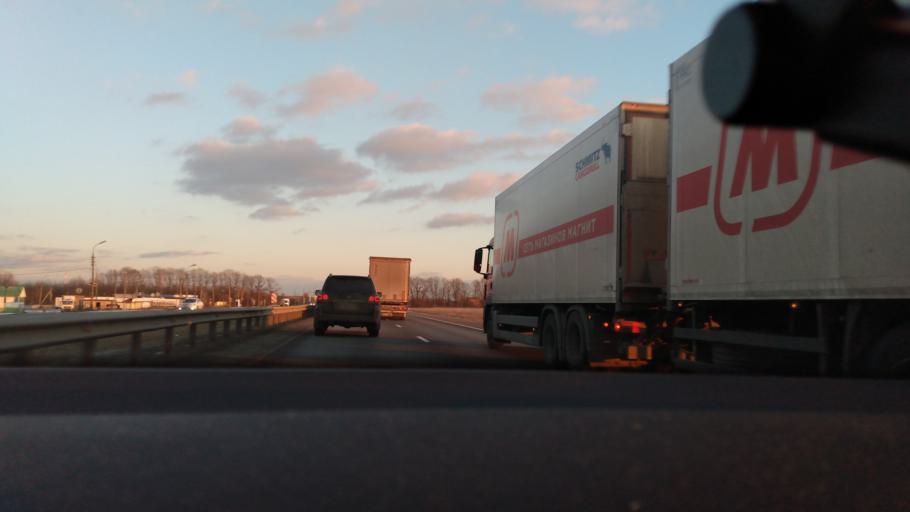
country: RU
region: Moskovskaya
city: Raduzhnyy
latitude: 55.1484
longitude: 38.7185
